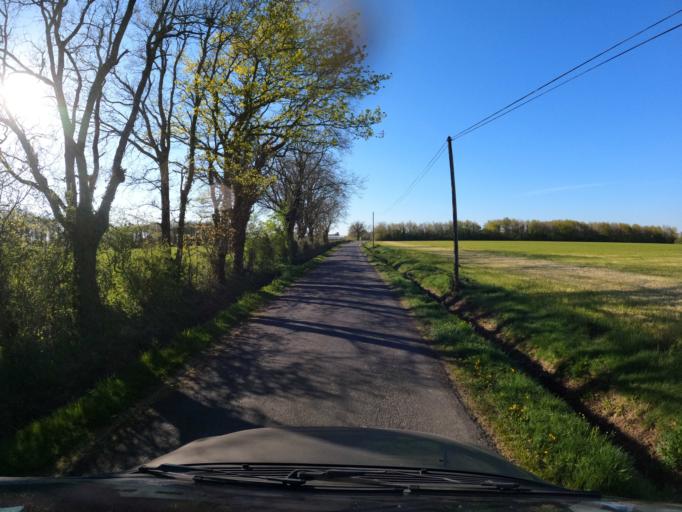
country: FR
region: Pays de la Loire
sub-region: Departement de la Vendee
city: Les Brouzils
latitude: 46.8973
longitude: -1.3699
